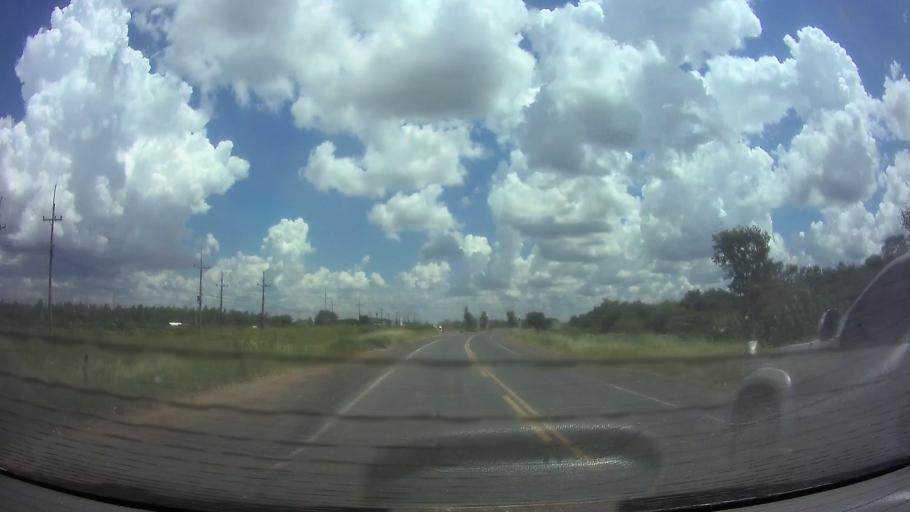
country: PY
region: Central
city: Colonia Mariano Roque Alonso
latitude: -25.1857
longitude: -57.5937
